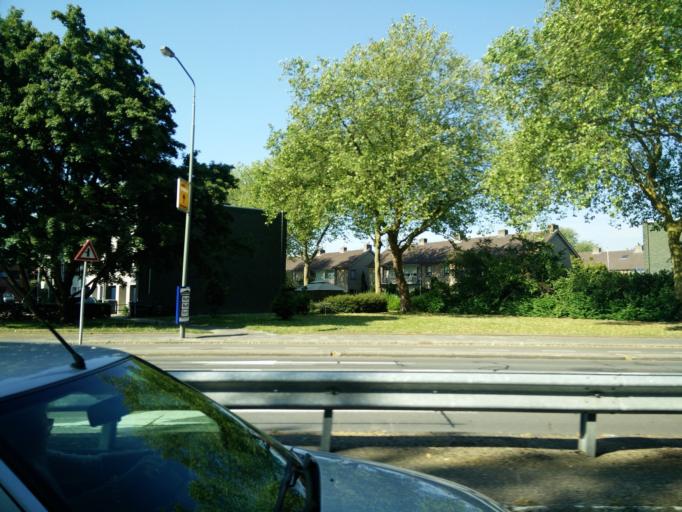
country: NL
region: South Holland
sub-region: Gemeente Dordrecht
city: Dordrecht
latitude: 51.7891
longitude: 4.6759
